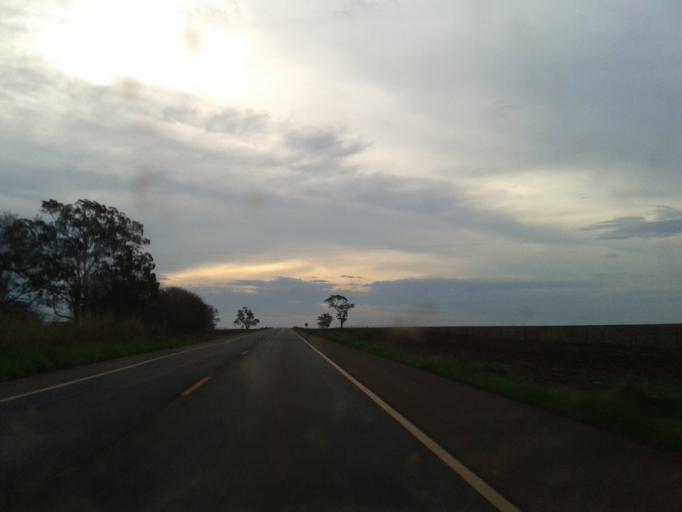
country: BR
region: Goias
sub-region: Santa Helena De Goias
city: Santa Helena de Goias
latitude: -17.8872
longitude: -50.6781
